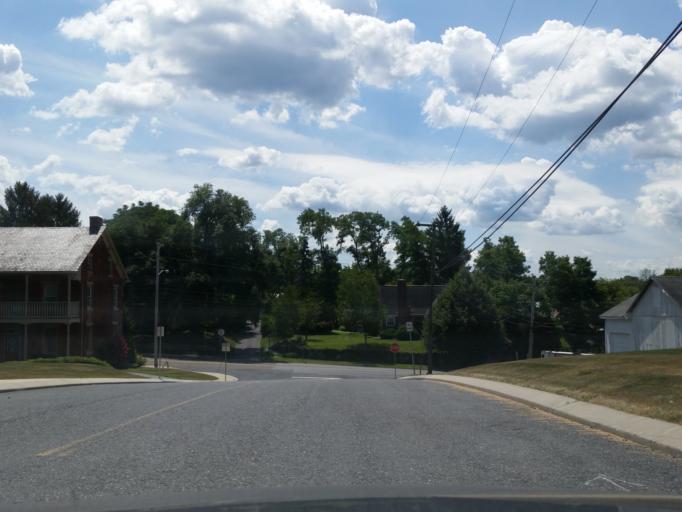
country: US
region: Pennsylvania
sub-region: Lebanon County
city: Annville
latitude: 40.3284
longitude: -76.5246
